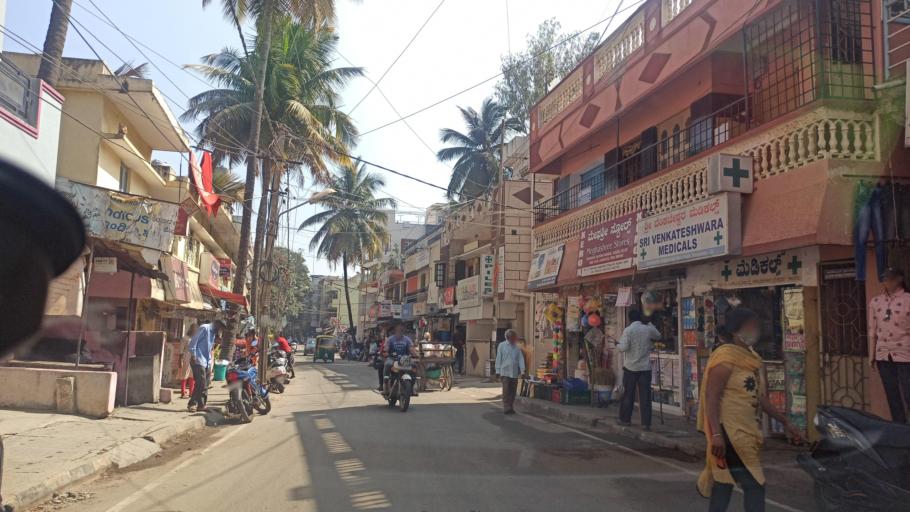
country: IN
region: Karnataka
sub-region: Bangalore Urban
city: Yelahanka
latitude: 13.0390
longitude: 77.5988
